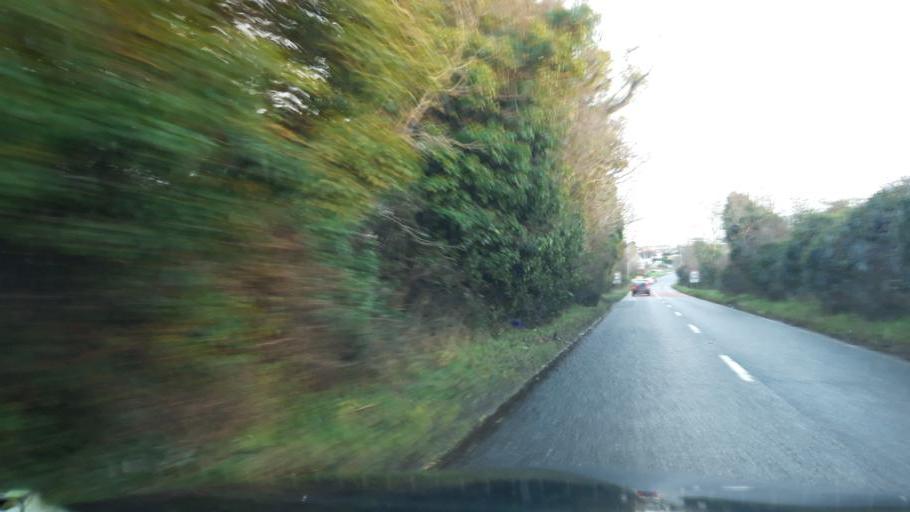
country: GB
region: Northern Ireland
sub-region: Moyle District
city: Ballycastle
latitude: 55.1937
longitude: -6.2682
